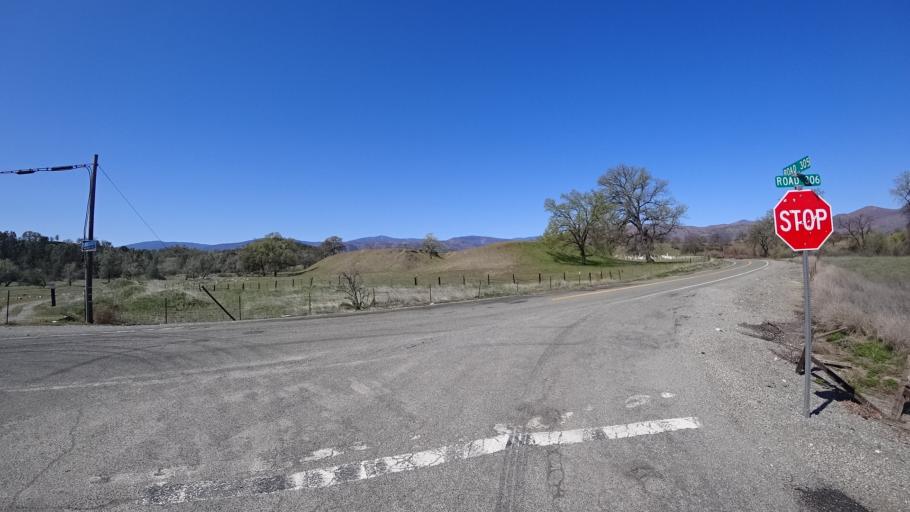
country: US
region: California
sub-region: Glenn County
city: Orland
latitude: 39.6801
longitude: -122.5317
